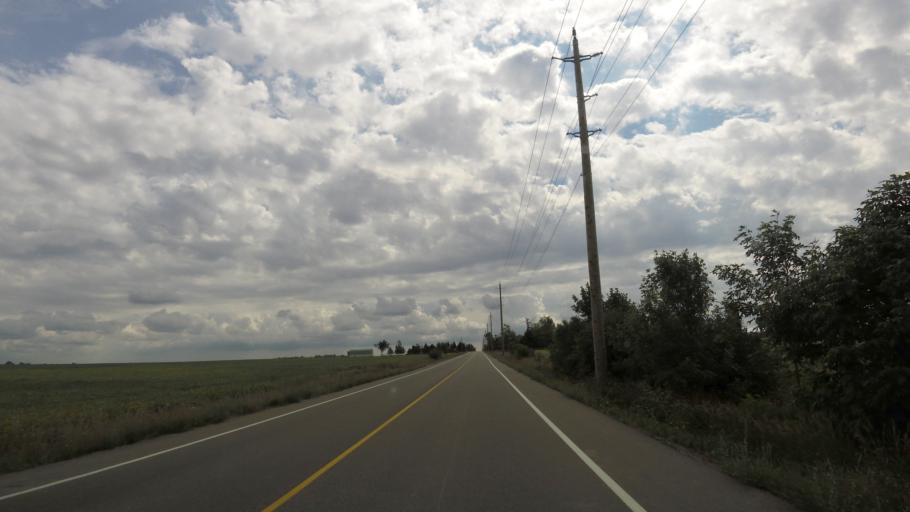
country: CA
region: Ontario
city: Brampton
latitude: 43.7112
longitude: -79.8659
